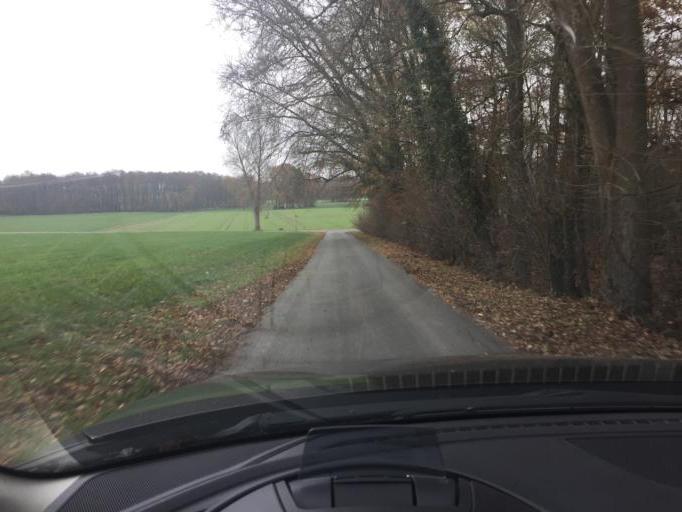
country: DE
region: North Rhine-Westphalia
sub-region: Regierungsbezirk Dusseldorf
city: Schermbeck
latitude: 51.7091
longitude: 6.8647
